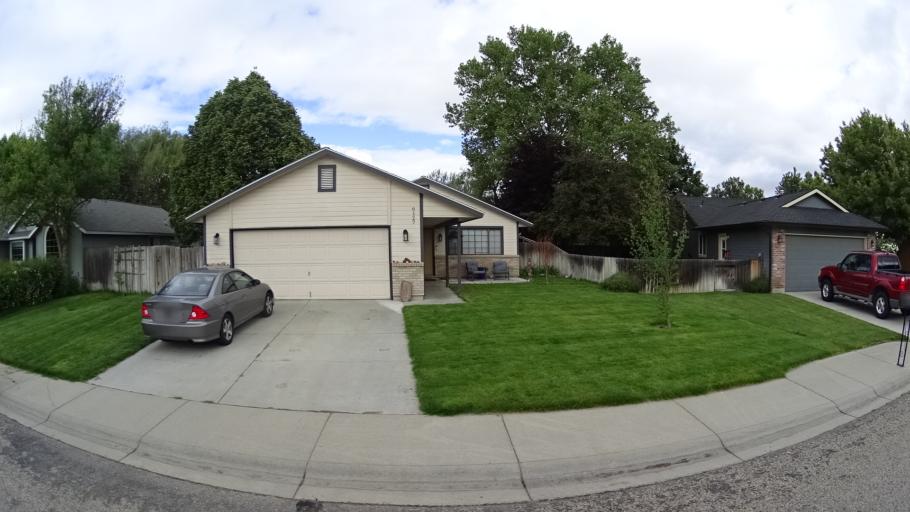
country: US
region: Idaho
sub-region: Ada County
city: Garden City
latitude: 43.6759
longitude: -116.2734
